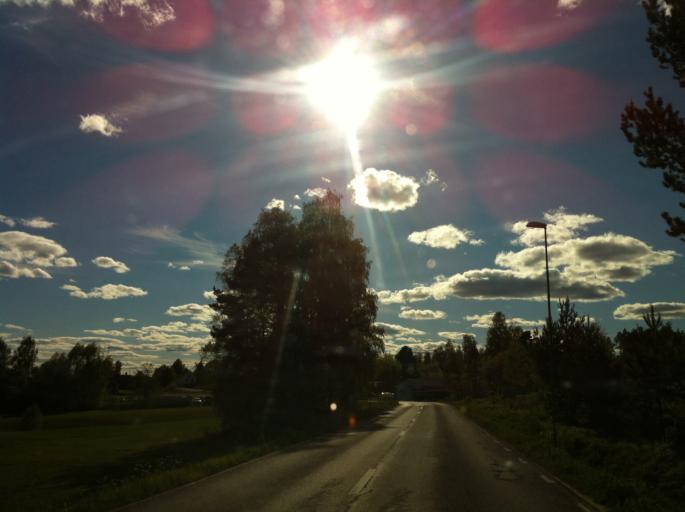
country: SE
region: Dalarna
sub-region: Leksand Municipality
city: Siljansnas
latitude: 60.7723
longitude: 14.8839
